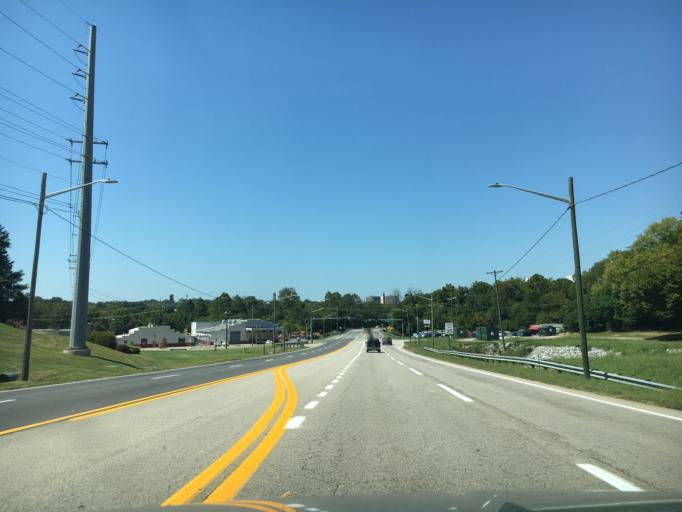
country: US
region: Virginia
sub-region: City of Danville
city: Danville
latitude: 36.5868
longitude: -79.3757
